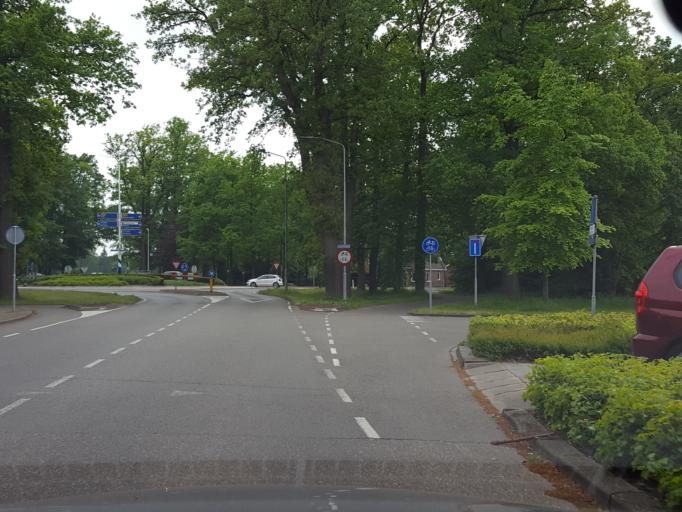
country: NL
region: Gelderland
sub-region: Gemeente Winterswijk
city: Winterswijk
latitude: 51.9612
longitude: 6.7212
